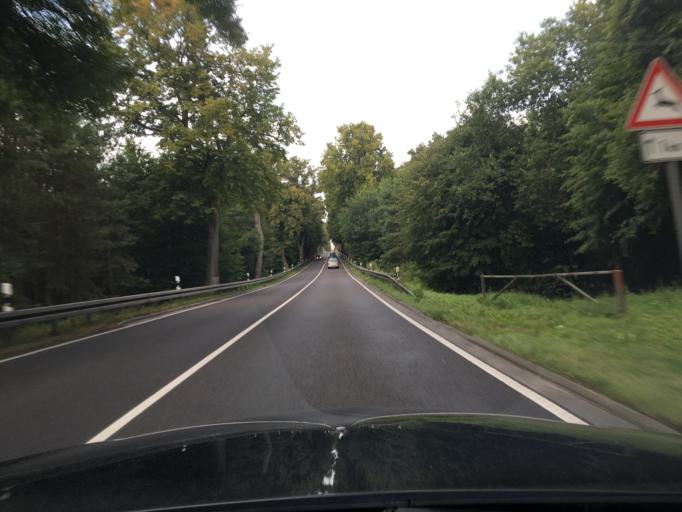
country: DE
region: Mecklenburg-Vorpommern
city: Wustrow
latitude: 53.4513
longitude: 13.1860
